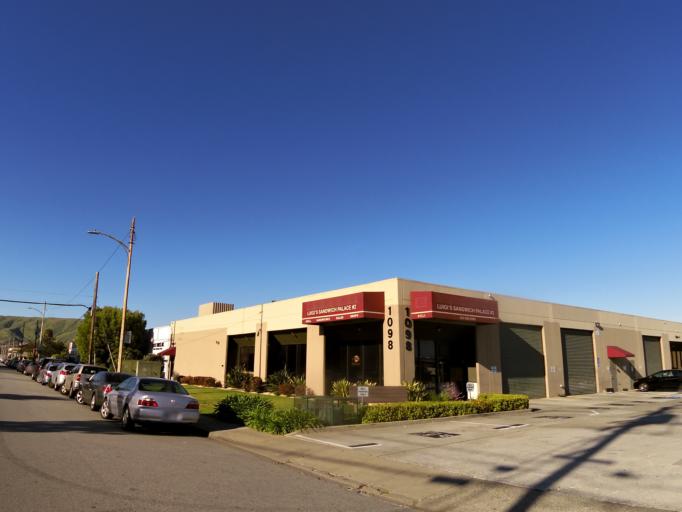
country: US
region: California
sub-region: San Mateo County
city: San Bruno
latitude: 37.6367
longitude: -122.4115
